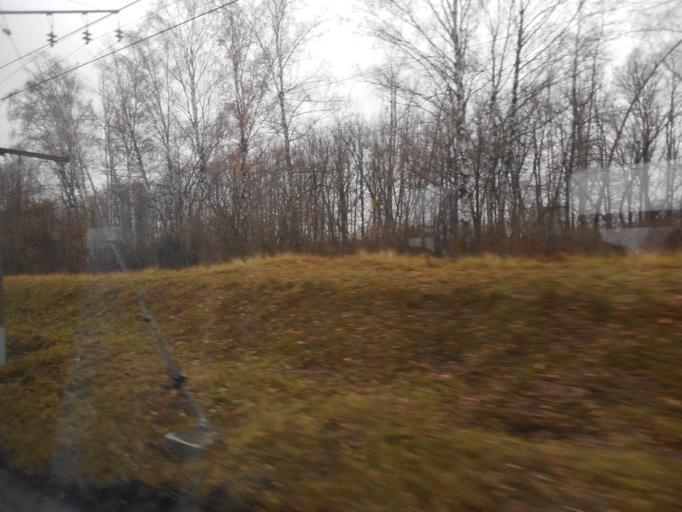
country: RU
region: Moskovskaya
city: Vidnoye
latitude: 55.5354
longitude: 37.6964
